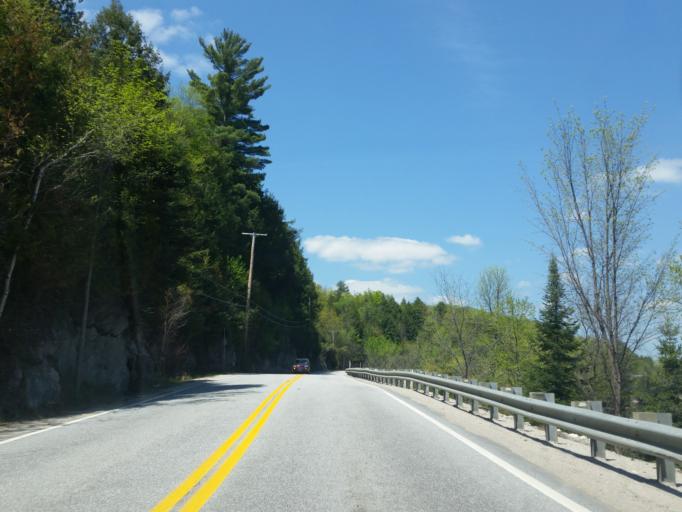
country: CA
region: Quebec
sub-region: Outaouais
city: Wakefield
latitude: 45.6534
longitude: -75.9254
